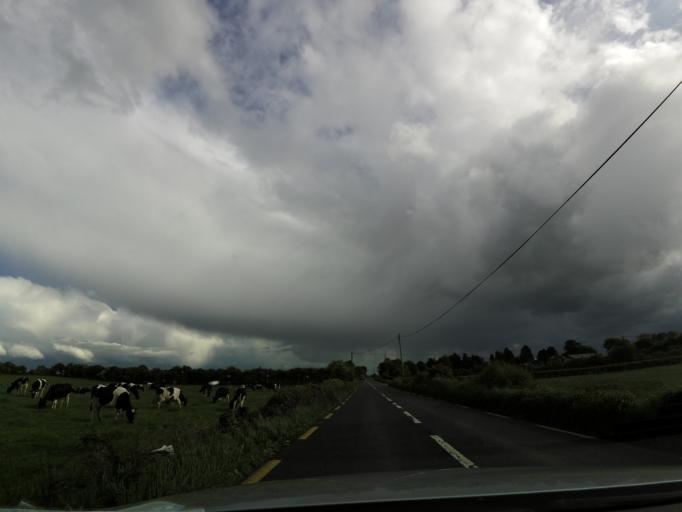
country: IE
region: Munster
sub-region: North Tipperary
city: Templemore
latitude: 52.7470
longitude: -7.8452
